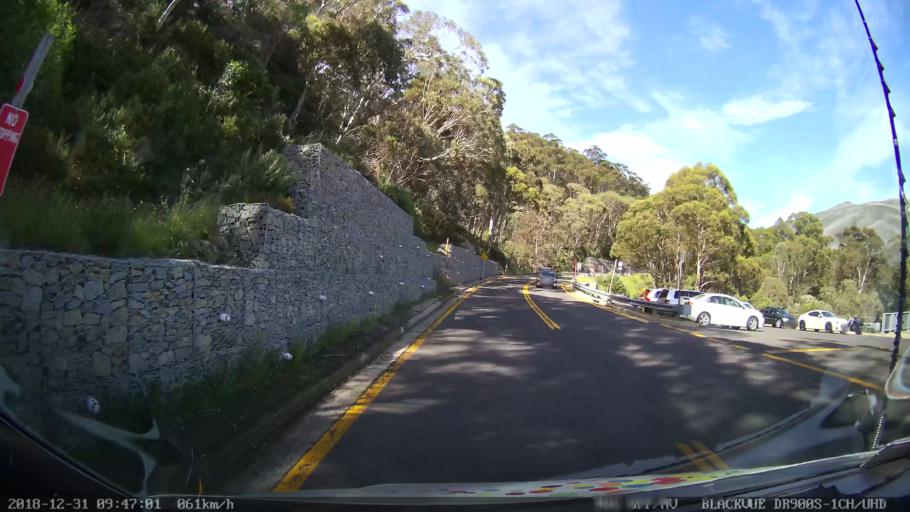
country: AU
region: New South Wales
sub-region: Snowy River
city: Jindabyne
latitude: -36.5069
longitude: 148.3051
